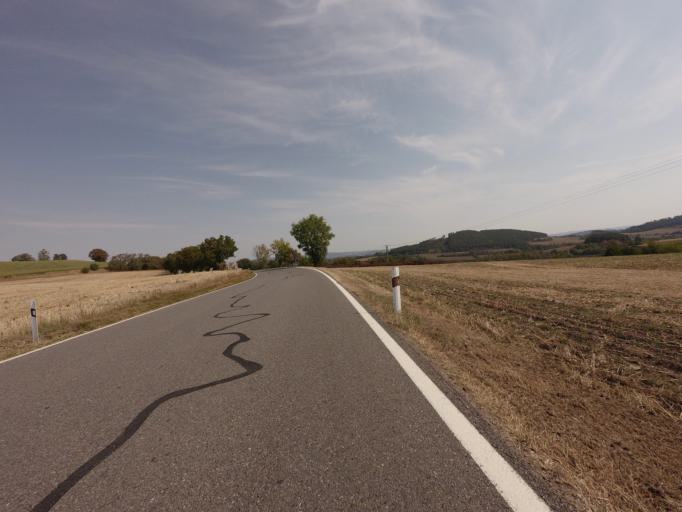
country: CZ
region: Central Bohemia
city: Petrovice
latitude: 49.5800
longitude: 14.3798
